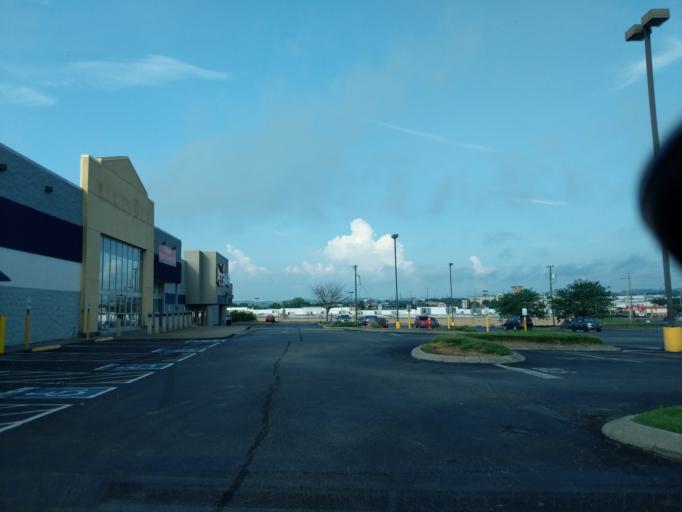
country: US
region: Tennessee
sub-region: Davidson County
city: Goodlettsville
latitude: 36.3041
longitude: -86.6879
